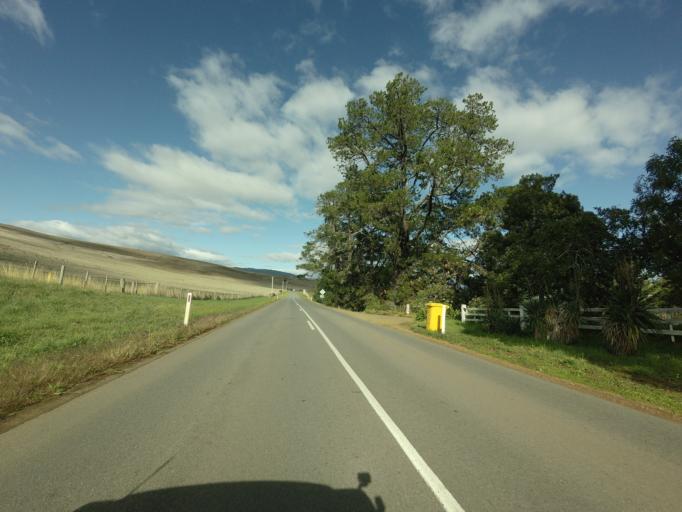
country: AU
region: Tasmania
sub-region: Derwent Valley
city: New Norfolk
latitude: -42.6939
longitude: 146.9341
